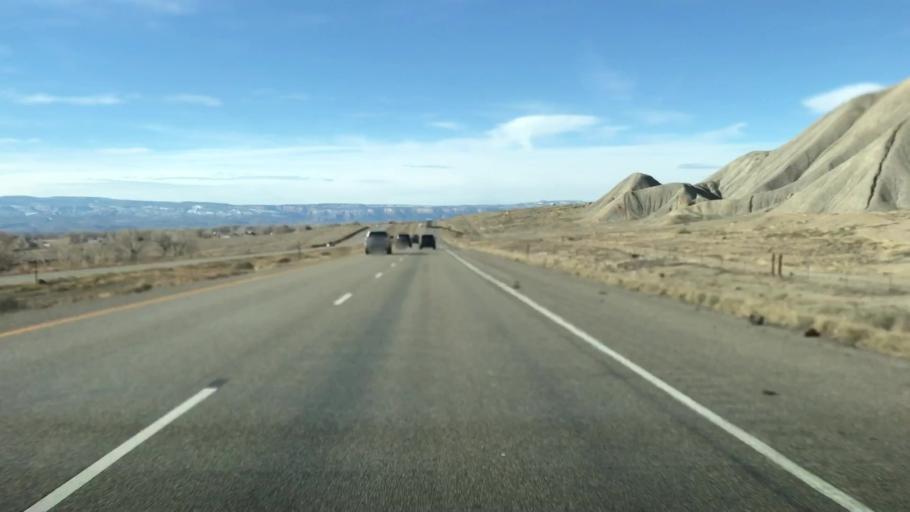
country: US
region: Colorado
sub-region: Mesa County
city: Palisade
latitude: 39.1148
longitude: -108.4017
